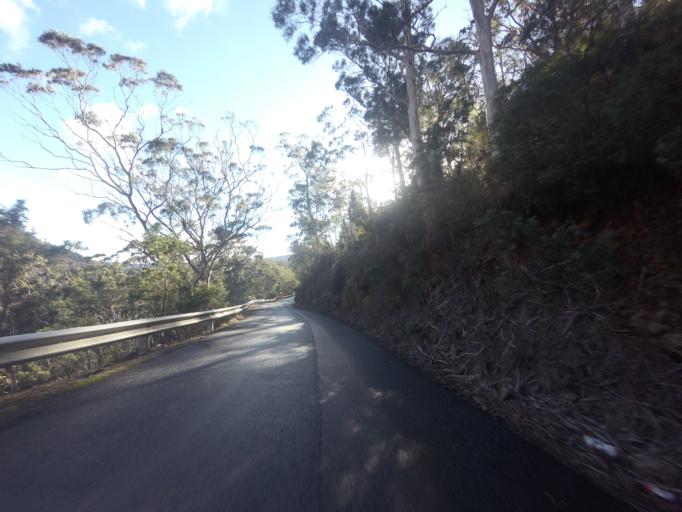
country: AU
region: Tasmania
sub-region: Glenorchy
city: Berriedale
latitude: -42.8208
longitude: 147.1799
